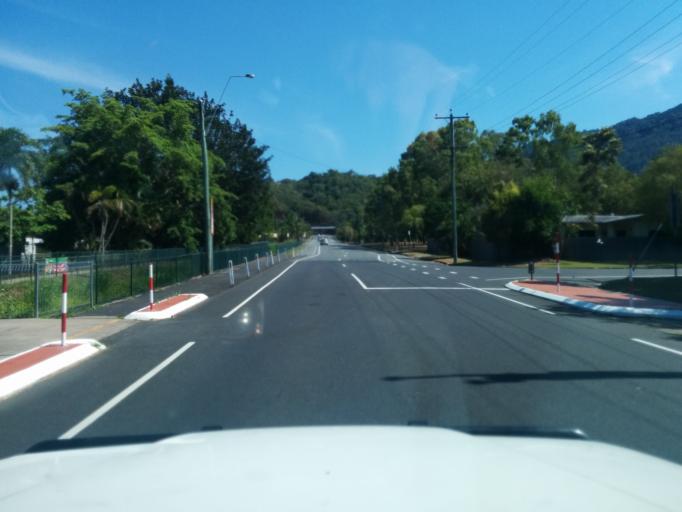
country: AU
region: Queensland
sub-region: Cairns
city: Redlynch
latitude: -16.9102
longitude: 145.7282
